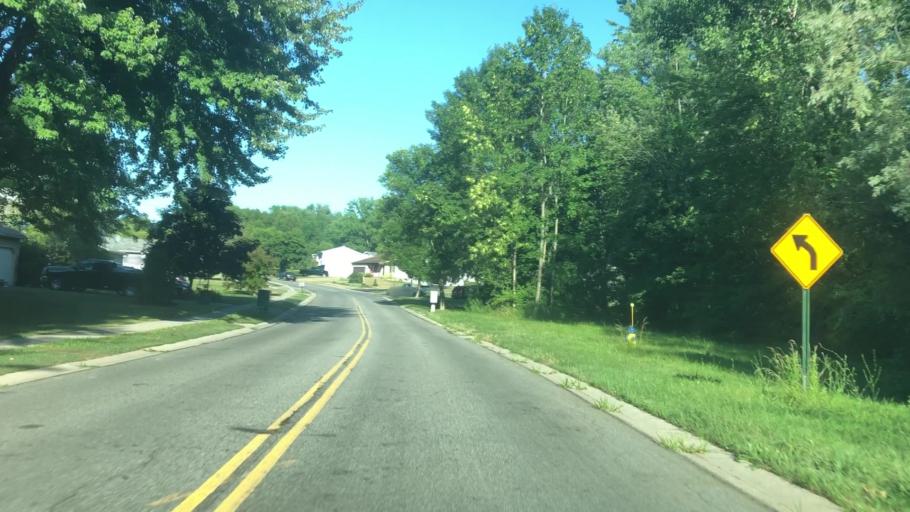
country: US
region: New York
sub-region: Wayne County
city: Macedon
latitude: 43.1240
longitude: -77.3016
